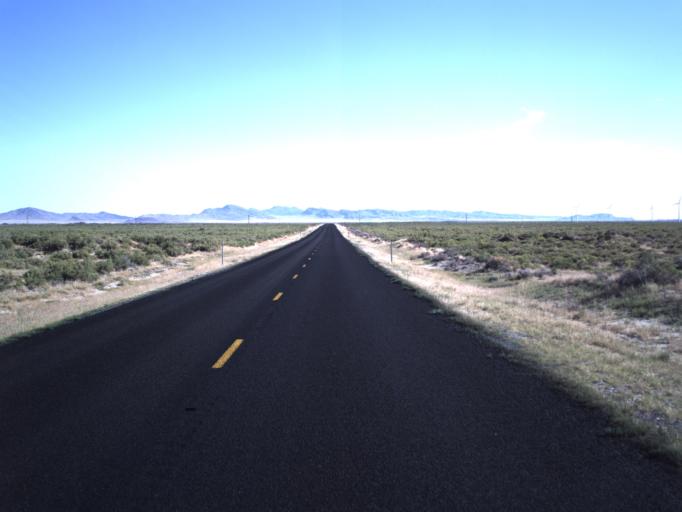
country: US
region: Utah
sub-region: Beaver County
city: Milford
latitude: 38.5466
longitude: -112.9912
